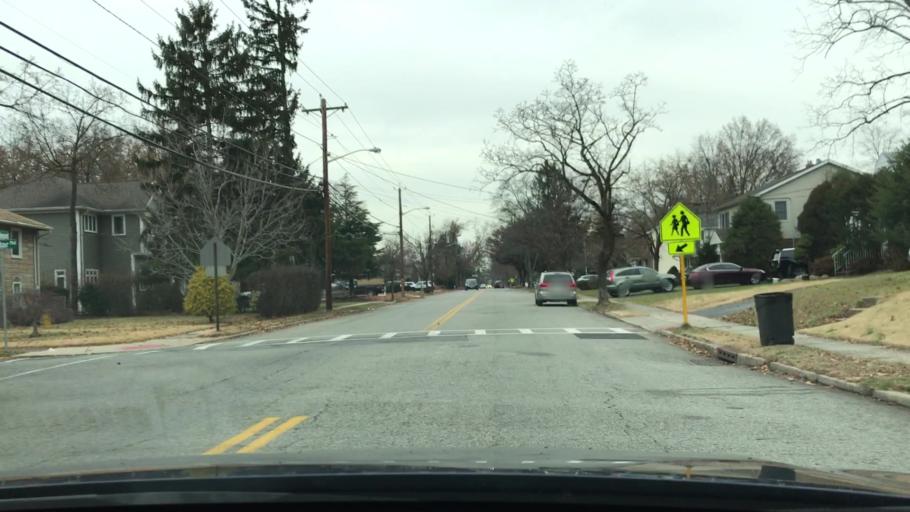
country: US
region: New Jersey
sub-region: Bergen County
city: New Milford
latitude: 40.9354
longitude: -74.0168
